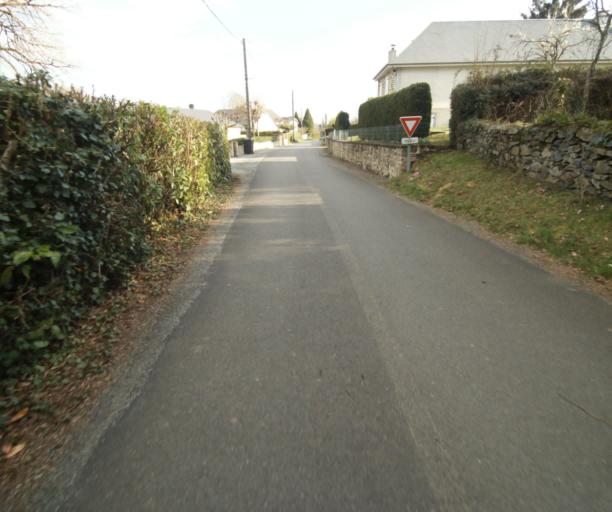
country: FR
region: Limousin
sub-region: Departement de la Correze
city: Saint-Clement
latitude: 45.3492
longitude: 1.6373
